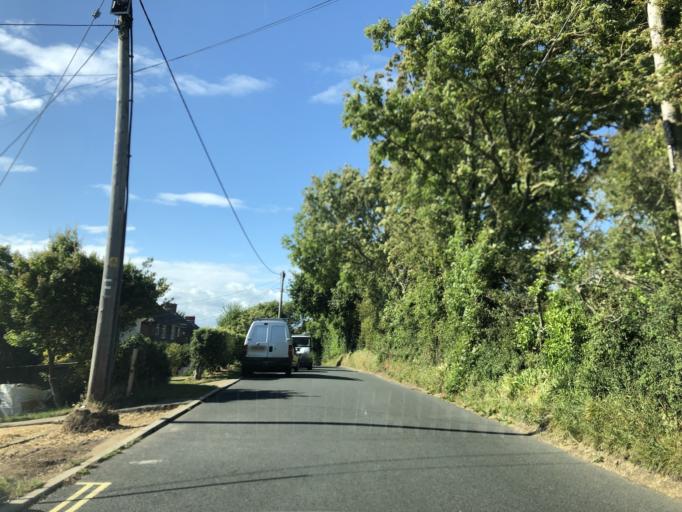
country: GB
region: England
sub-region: Isle of Wight
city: Shalfleet
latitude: 50.6809
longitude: -1.3997
